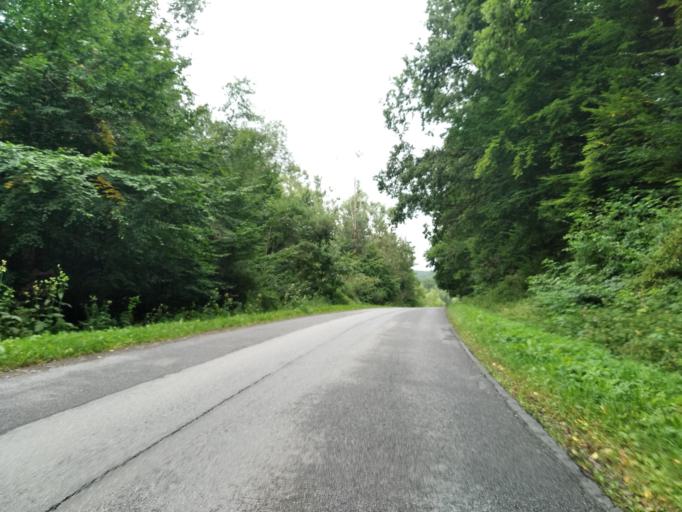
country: PL
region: Subcarpathian Voivodeship
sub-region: Powiat przemyski
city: Bircza
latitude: 49.6804
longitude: 22.4147
